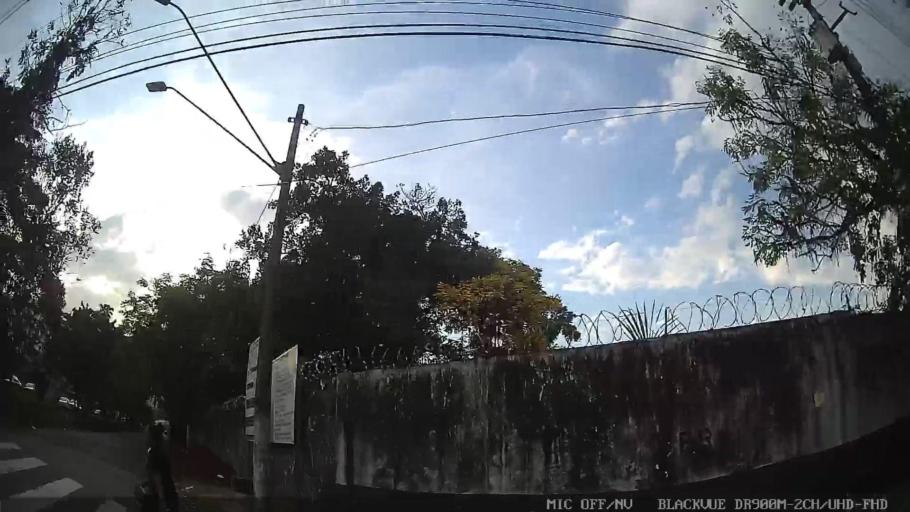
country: BR
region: Sao Paulo
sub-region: Cubatao
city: Cubatao
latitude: -23.8920
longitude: -46.4256
